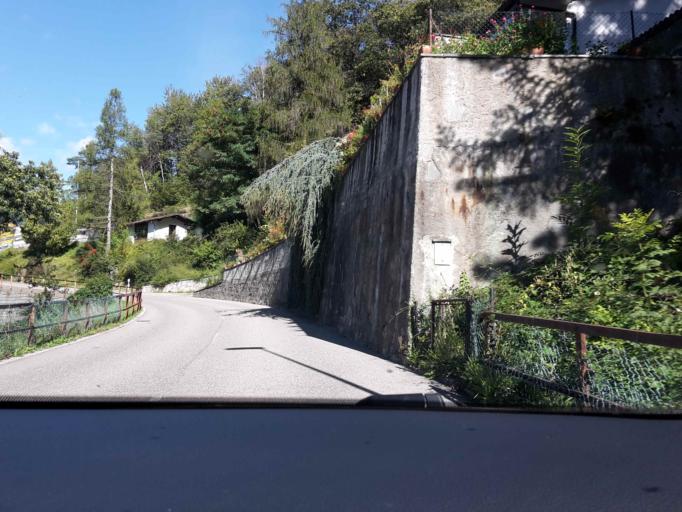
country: CH
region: Ticino
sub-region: Bellinzona District
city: Giubiasco
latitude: 46.1725
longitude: 9.0293
